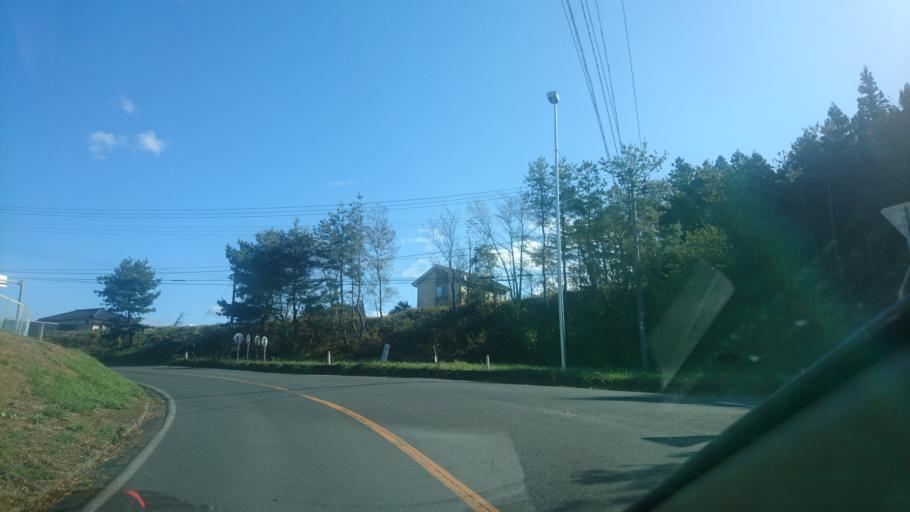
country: JP
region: Iwate
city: Ofunato
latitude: 38.9932
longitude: 141.7068
